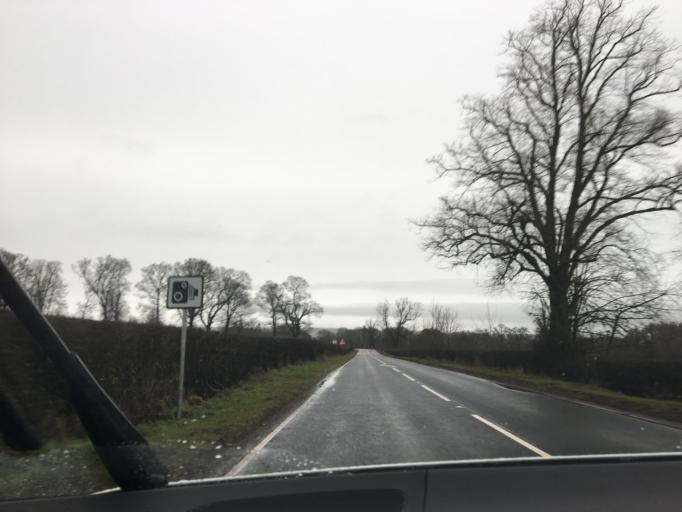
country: GB
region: Scotland
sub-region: Stirling
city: Doune
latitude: 56.1749
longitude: -4.0636
